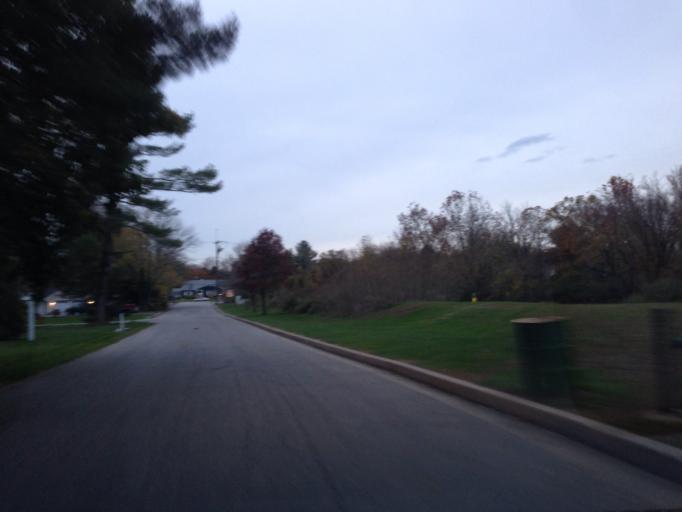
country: US
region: Maryland
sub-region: Baltimore County
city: Mays Chapel
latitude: 39.4148
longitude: -76.6442
